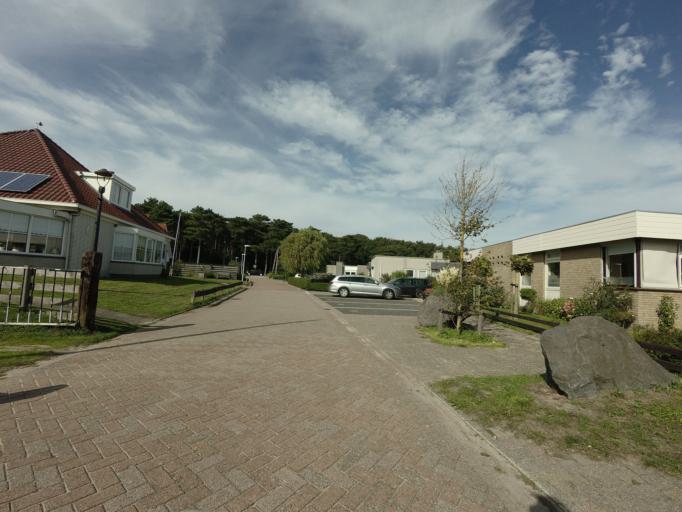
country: NL
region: North Holland
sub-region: Gemeente Texel
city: Den Burg
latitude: 53.1022
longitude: 4.7665
